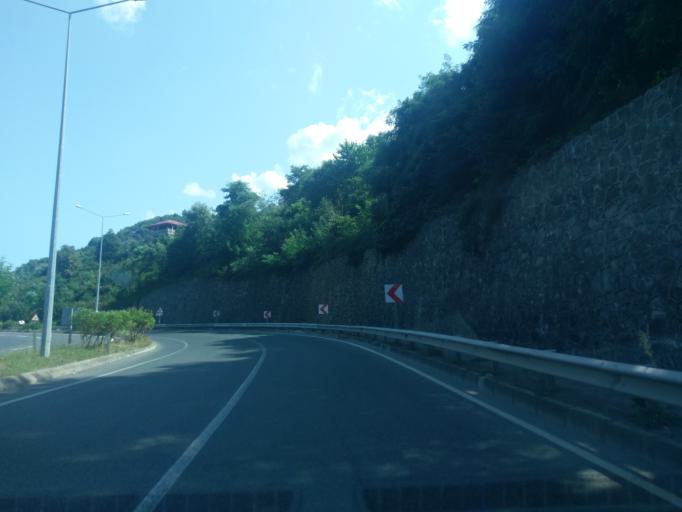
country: TR
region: Ordu
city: Ordu
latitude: 41.0166
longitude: 37.8458
